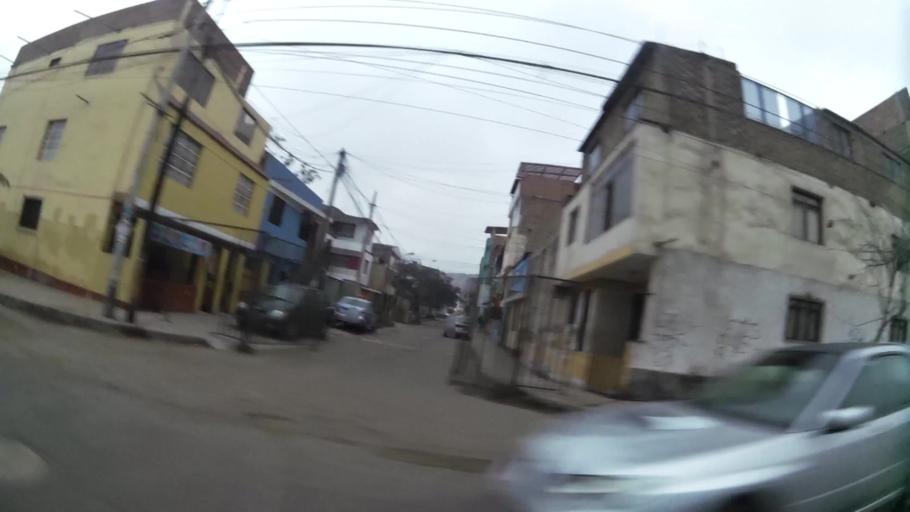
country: PE
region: Lima
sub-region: Lima
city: Surco
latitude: -12.1479
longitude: -76.9740
